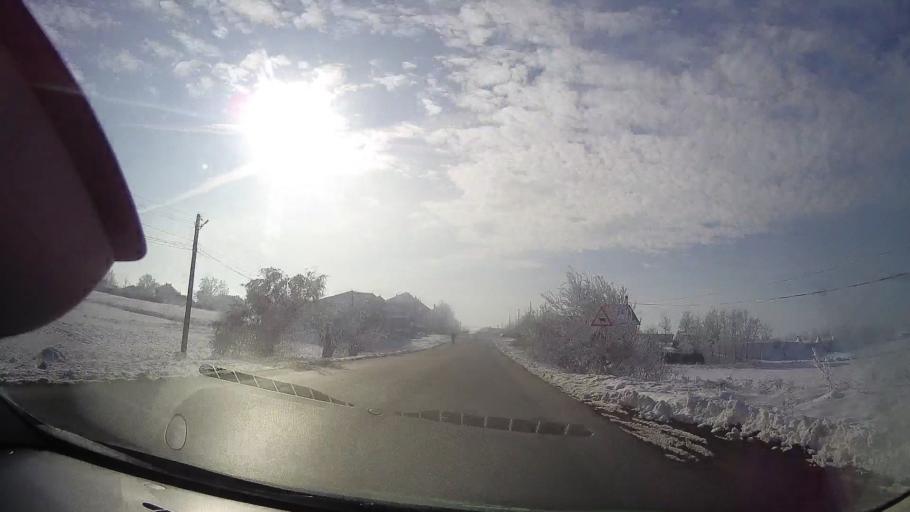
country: RO
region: Neamt
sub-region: Comuna Timisesti
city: Timisesti
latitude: 47.2372
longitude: 26.5363
